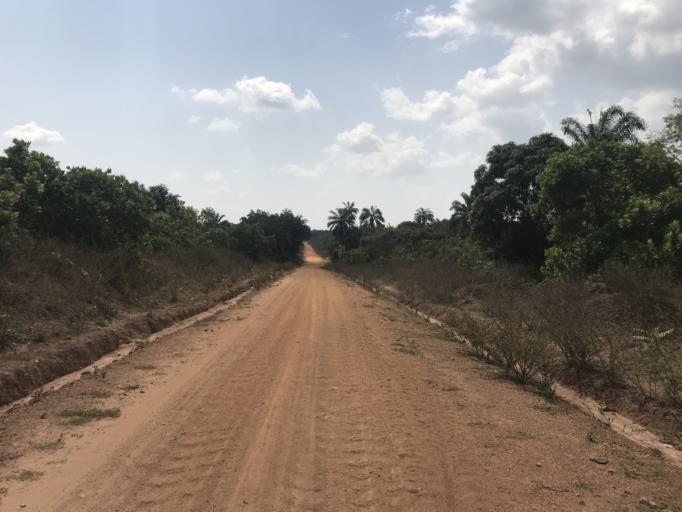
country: NG
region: Osun
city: Ifon
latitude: 7.9785
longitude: 4.5150
